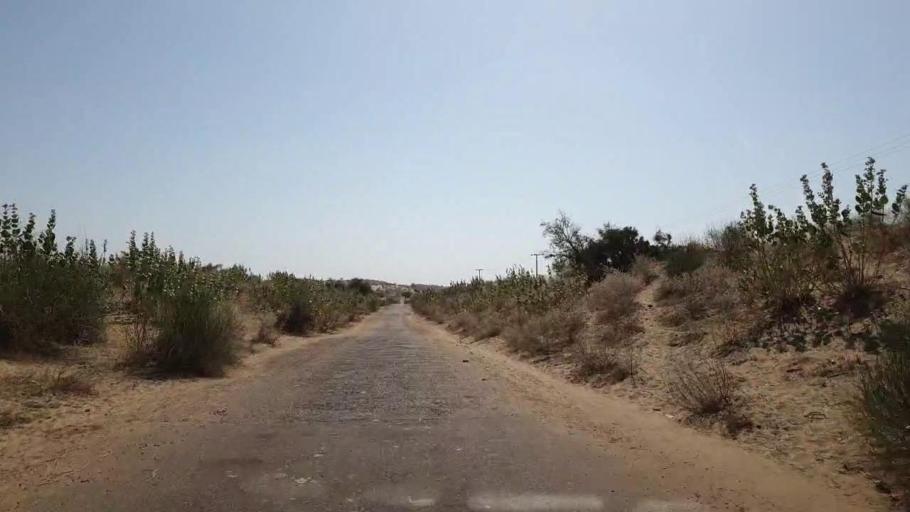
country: PK
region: Sindh
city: Umarkot
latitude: 25.1613
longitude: 70.0393
